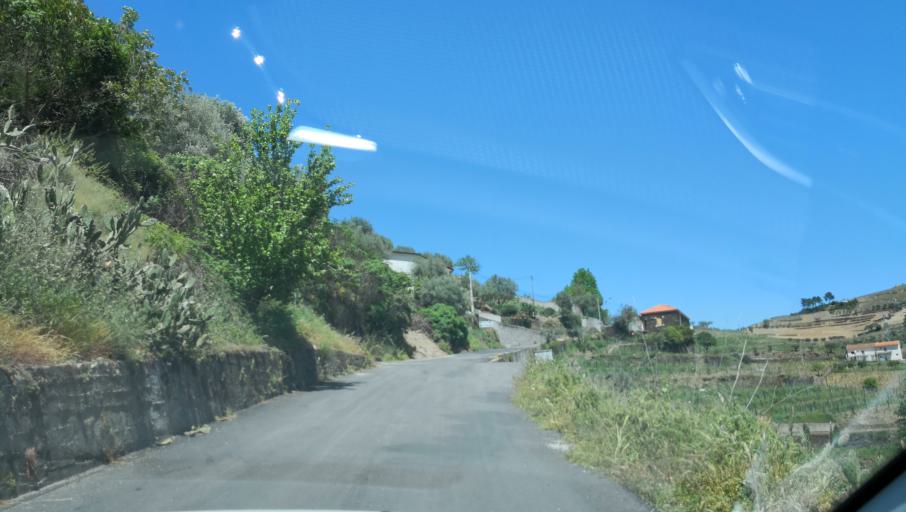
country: PT
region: Vila Real
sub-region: Santa Marta de Penaguiao
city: Santa Marta de Penaguiao
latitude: 41.2225
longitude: -7.7214
